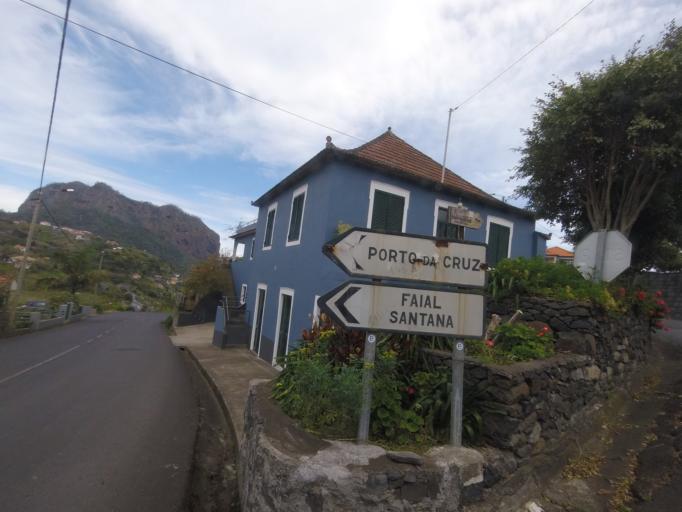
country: PT
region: Madeira
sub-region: Santana
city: Santana
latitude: 32.7587
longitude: -16.8293
